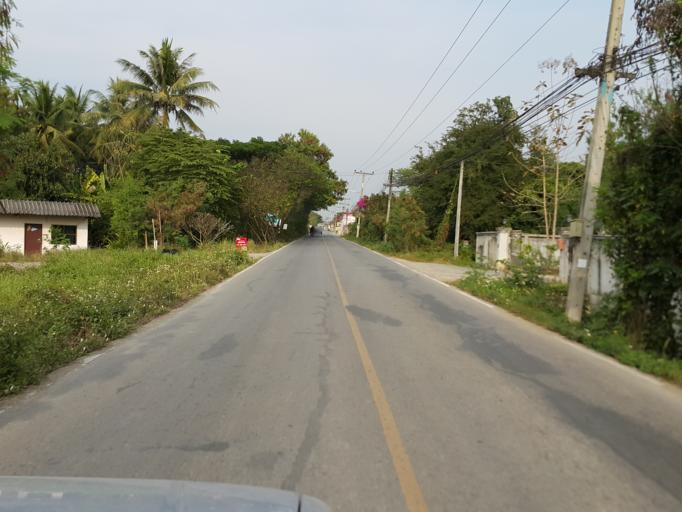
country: TH
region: Chiang Mai
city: Saraphi
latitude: 18.6949
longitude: 99.0087
